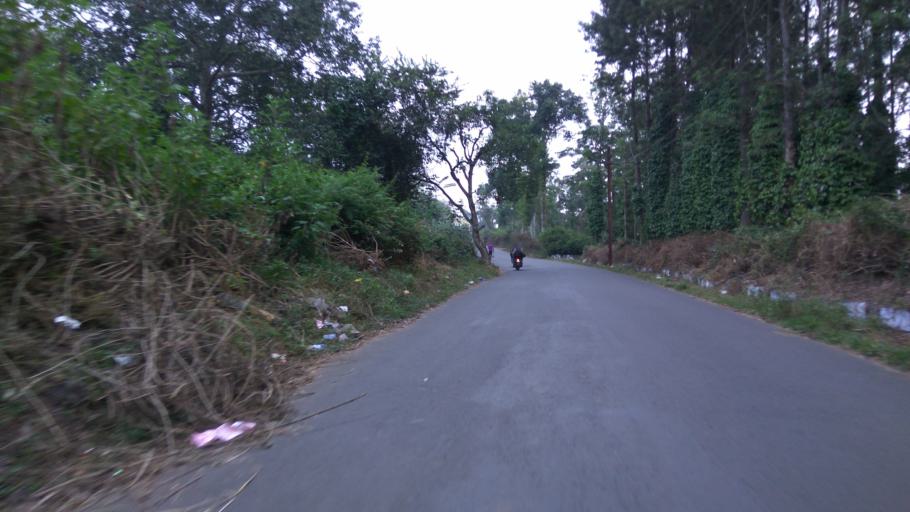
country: IN
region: Tamil Nadu
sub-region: Salem
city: Salem
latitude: 11.7801
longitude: 78.2104
